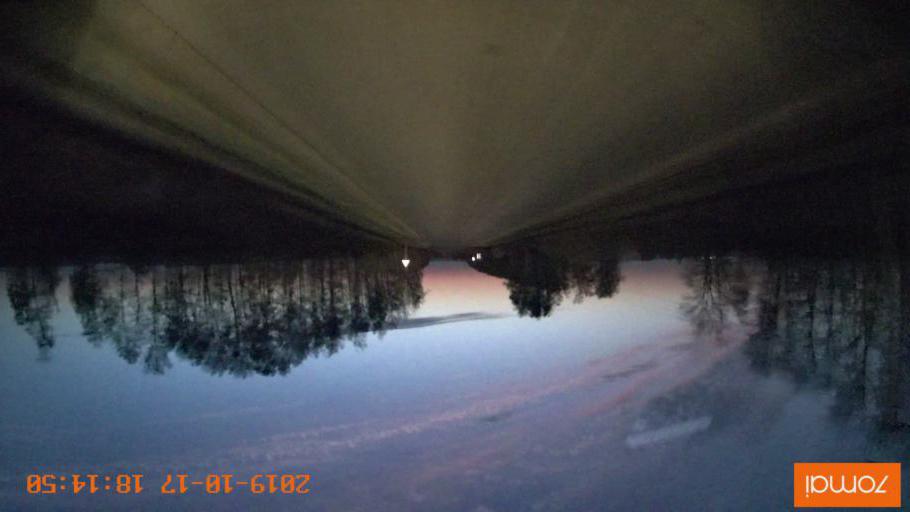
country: RU
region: Tula
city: Kurkino
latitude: 53.4060
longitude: 38.5524
